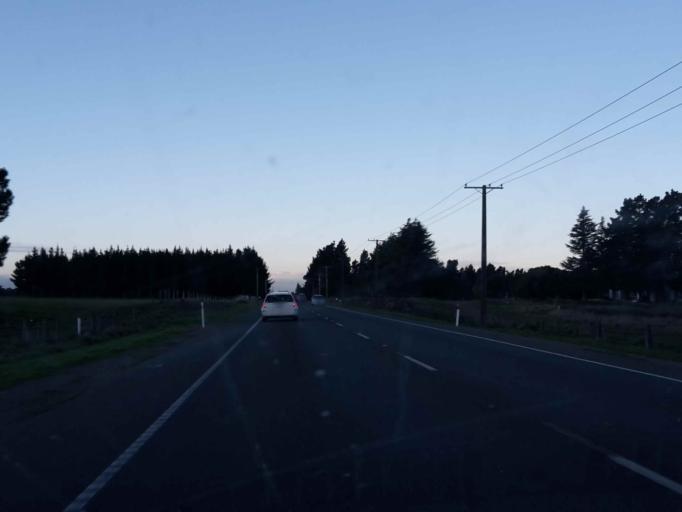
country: NZ
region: Canterbury
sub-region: Selwyn District
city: Prebbleton
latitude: -43.5647
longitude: 172.4502
